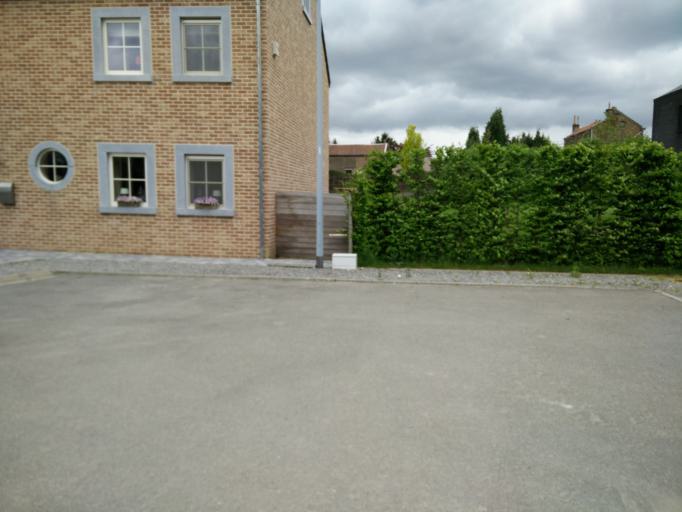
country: BE
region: Flanders
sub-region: Provincie Limburg
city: Sint-Pieters-Voeren
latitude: 50.7339
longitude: 5.7772
